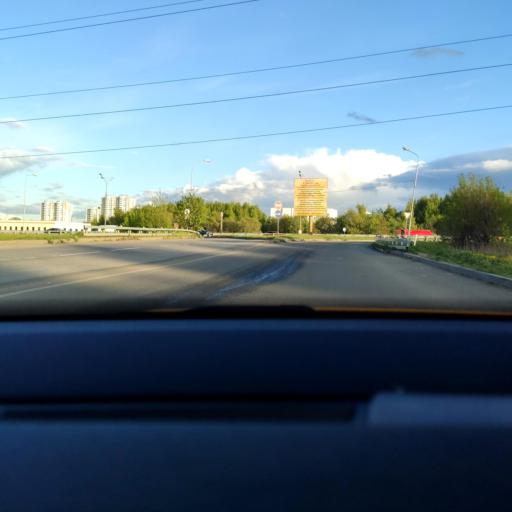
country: RU
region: Moscow
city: Lianozovo
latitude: 55.9116
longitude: 37.5696
